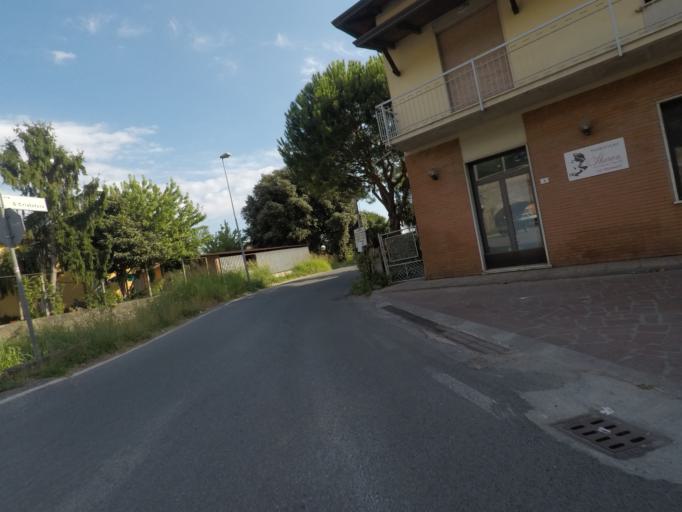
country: IT
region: Tuscany
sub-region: Provincia di Massa-Carrara
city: Capanne-Prato-Cinquale
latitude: 44.0136
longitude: 10.1497
